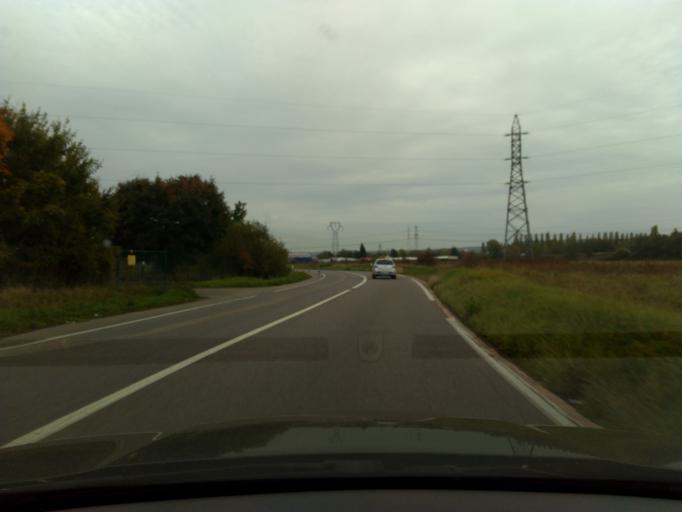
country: FR
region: Lorraine
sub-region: Departement de la Moselle
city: Maizieres-les-Metz
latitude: 49.2026
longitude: 6.1496
